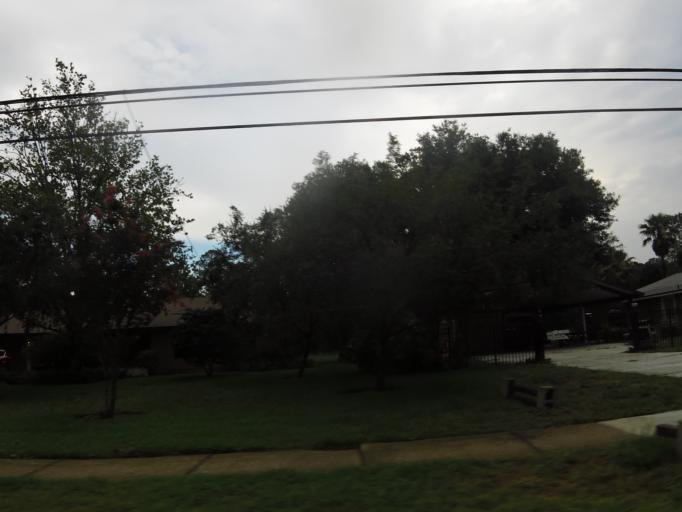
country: US
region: Florida
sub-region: Duval County
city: Jacksonville
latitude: 30.3138
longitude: -81.5418
